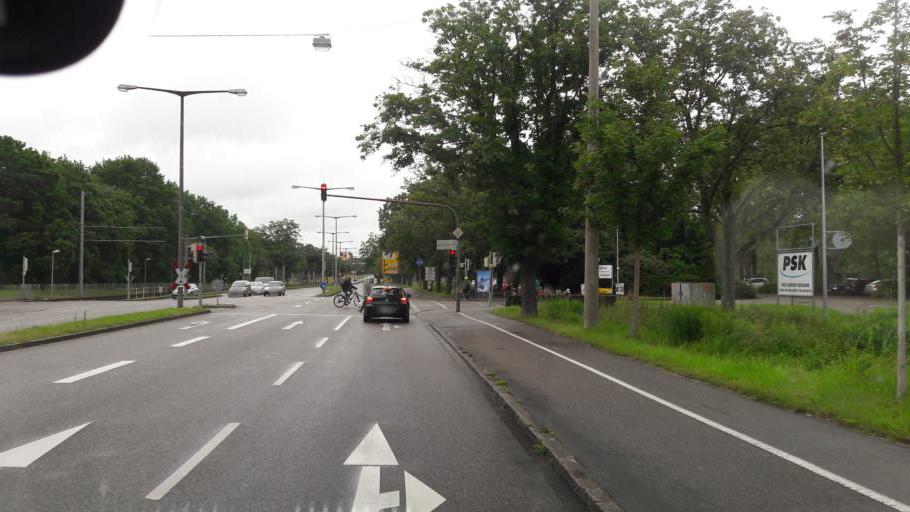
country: DE
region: Baden-Wuerttemberg
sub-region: Karlsruhe Region
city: Karlsruhe
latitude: 48.9844
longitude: 8.4040
